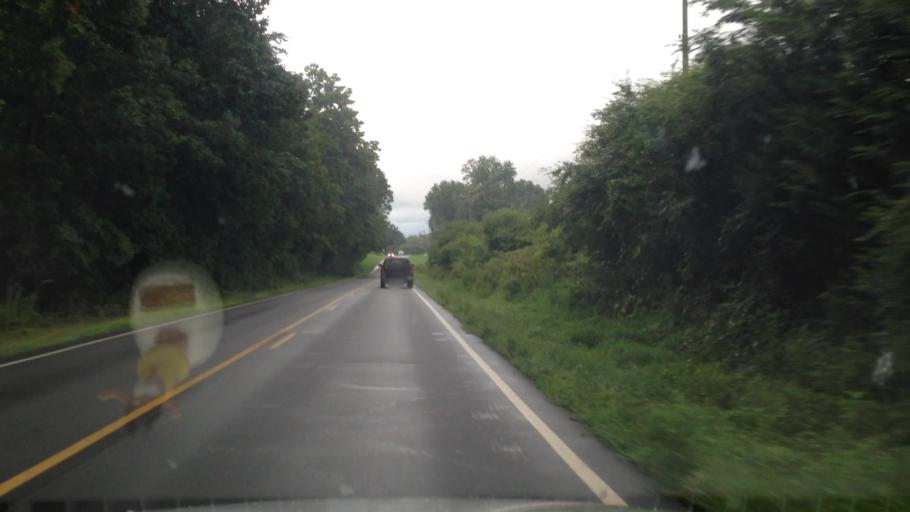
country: US
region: North Carolina
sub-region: Rockingham County
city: Reidsville
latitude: 36.2872
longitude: -79.7357
